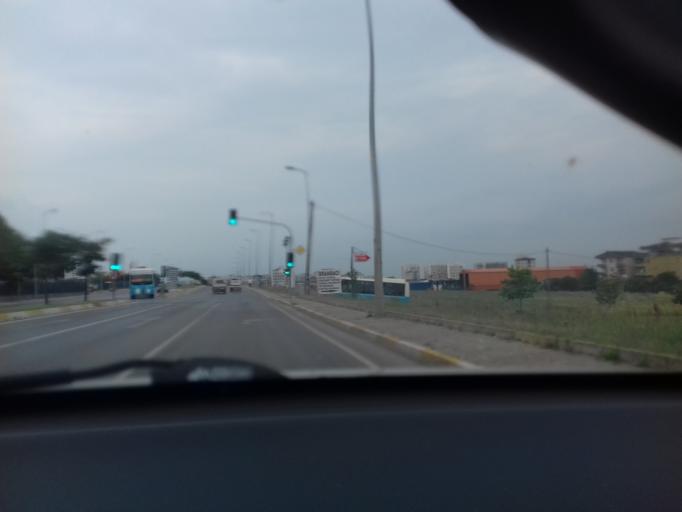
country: TR
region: Istanbul
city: Icmeler
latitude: 40.8787
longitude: 29.3413
